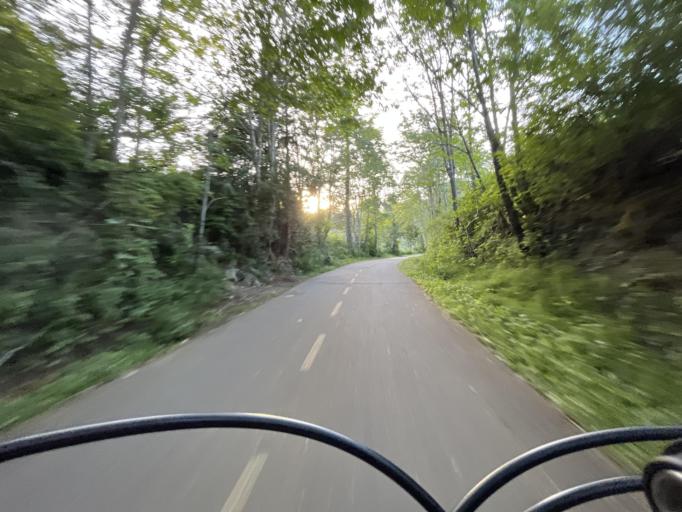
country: CA
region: British Columbia
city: Colwood
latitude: 48.4461
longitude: -123.4727
